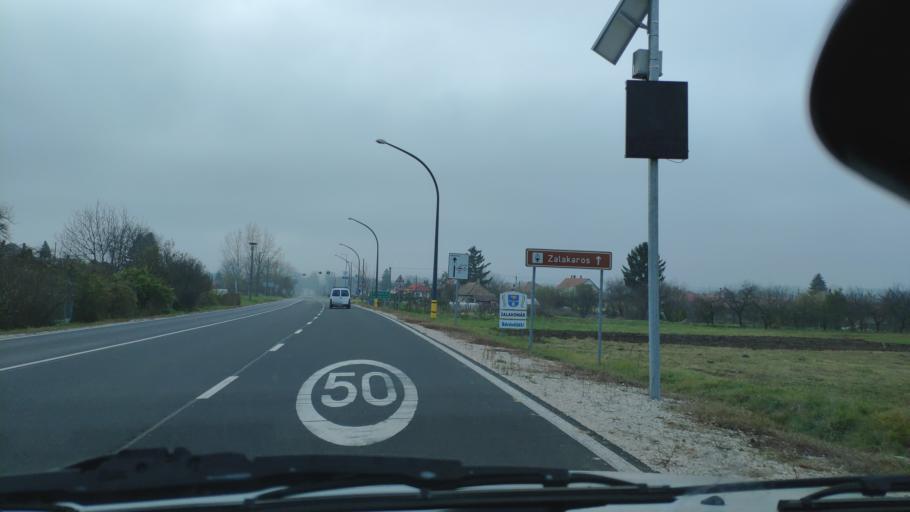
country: HU
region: Zala
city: Zalakomar
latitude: 46.5369
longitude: 17.1836
